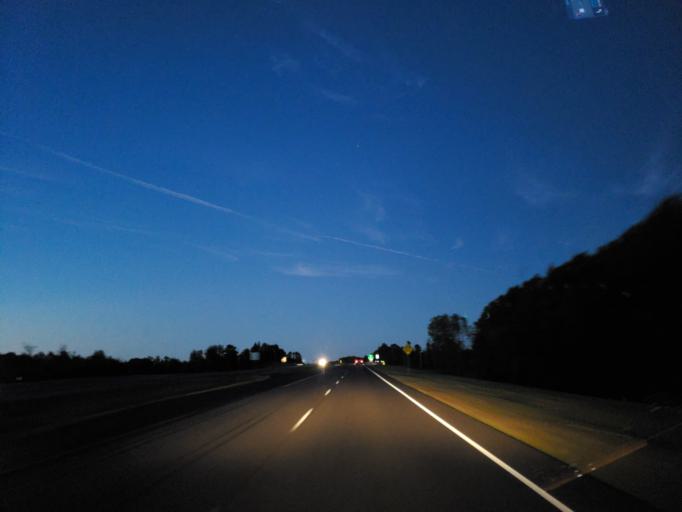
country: US
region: Mississippi
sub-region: Clarke County
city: Quitman
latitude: 32.0376
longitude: -88.6792
